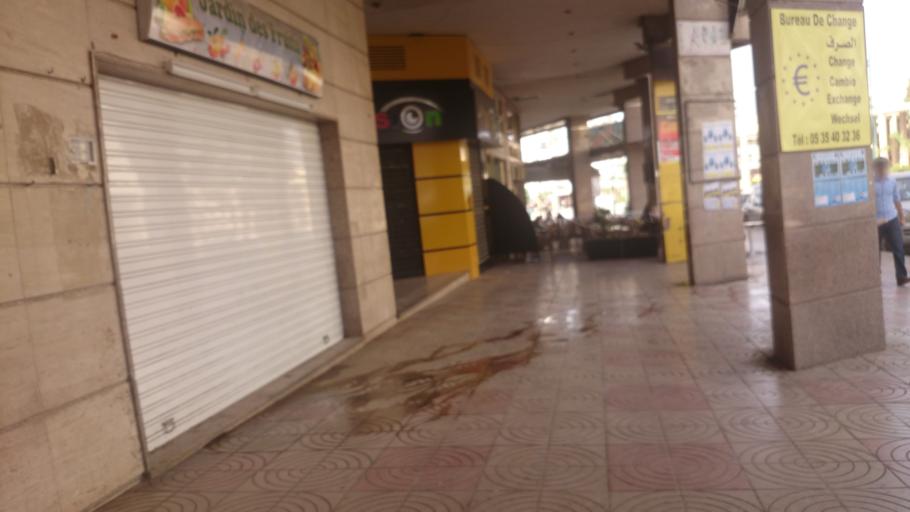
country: MA
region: Meknes-Tafilalet
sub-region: Meknes
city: Meknes
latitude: 33.8970
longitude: -5.5486
